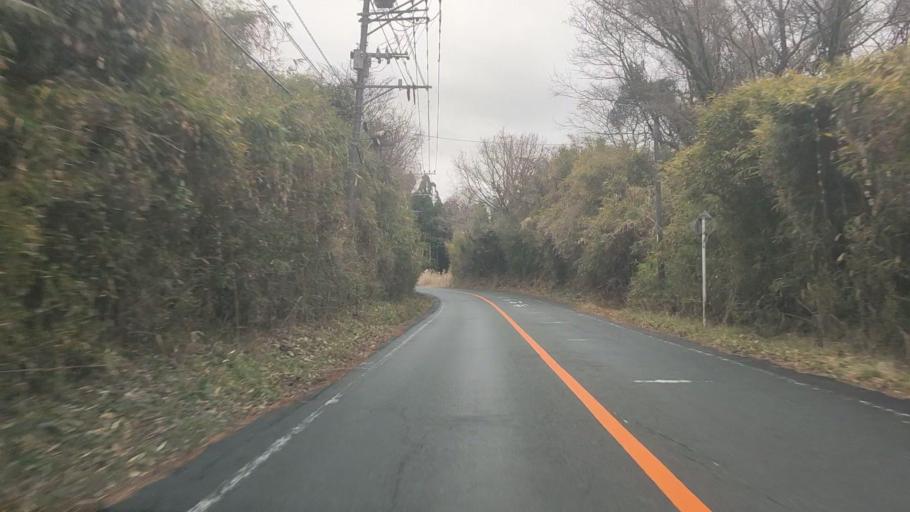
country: JP
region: Kumamoto
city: Aso
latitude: 32.8943
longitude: 131.0189
